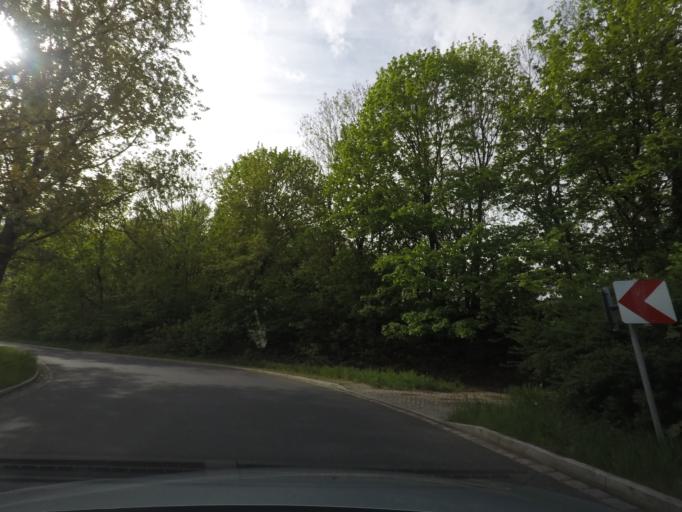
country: DE
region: Saxony
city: Dobeln
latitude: 51.1136
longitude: 13.1131
